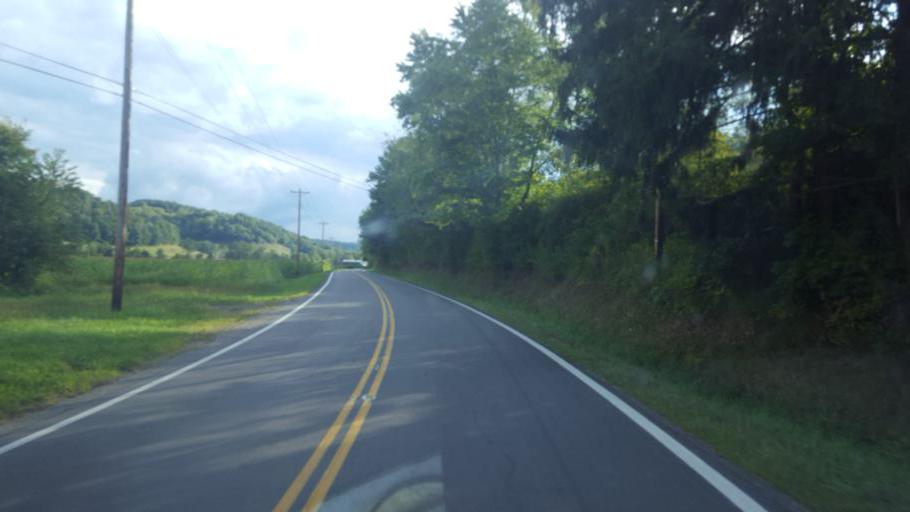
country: US
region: Ohio
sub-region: Holmes County
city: Millersburg
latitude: 40.4767
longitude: -82.0620
